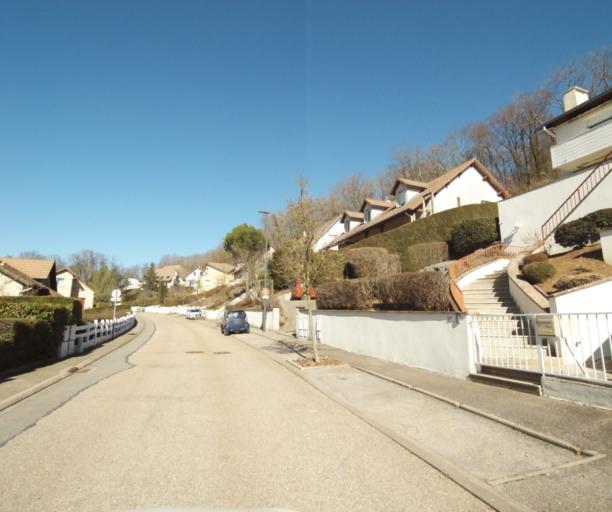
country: FR
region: Lorraine
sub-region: Departement de Meurthe-et-Moselle
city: Essey-les-Nancy
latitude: 48.7157
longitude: 6.2223
